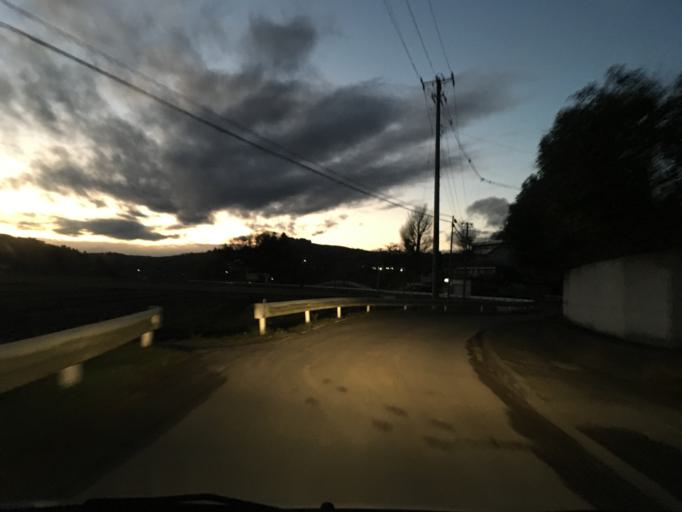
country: JP
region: Iwate
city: Ichinoseki
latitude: 38.8512
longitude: 141.2920
